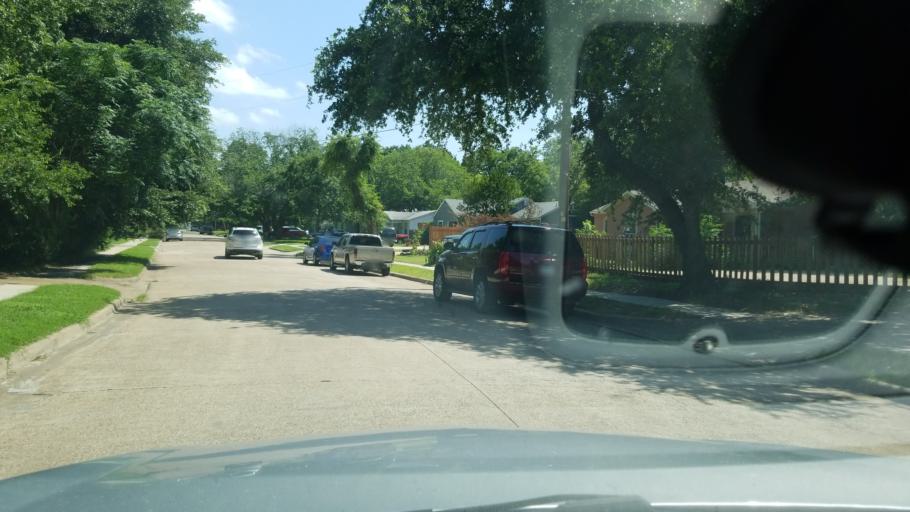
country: US
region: Texas
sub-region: Dallas County
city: Irving
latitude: 32.8201
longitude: -96.9582
